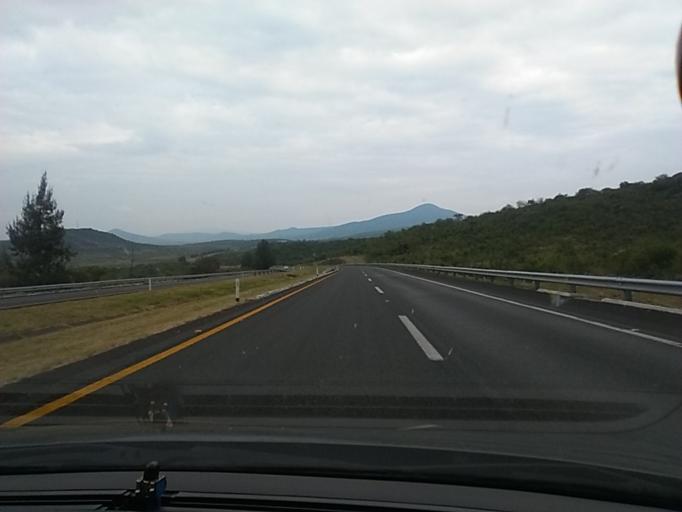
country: MX
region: Michoacan
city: Panindicuaro de la Reforma
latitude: 19.9968
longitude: -101.8300
